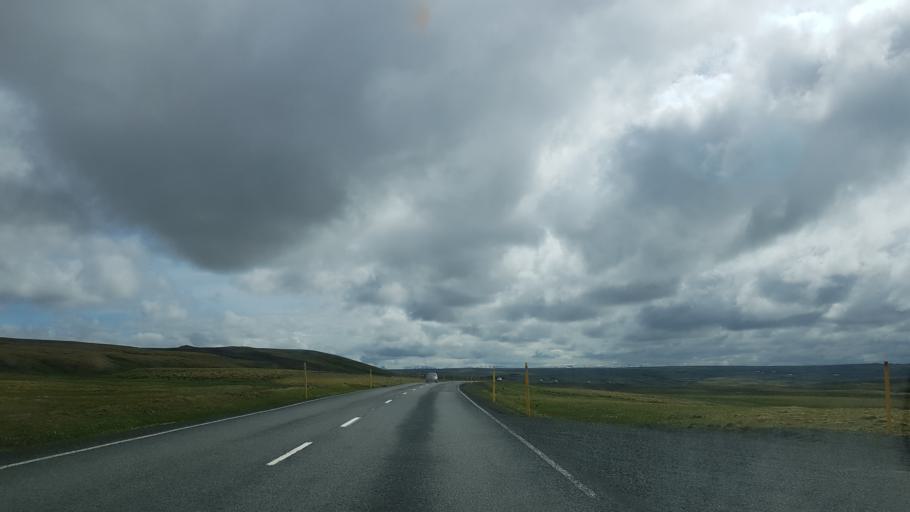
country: IS
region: West
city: Borgarnes
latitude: 64.9649
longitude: -21.0625
